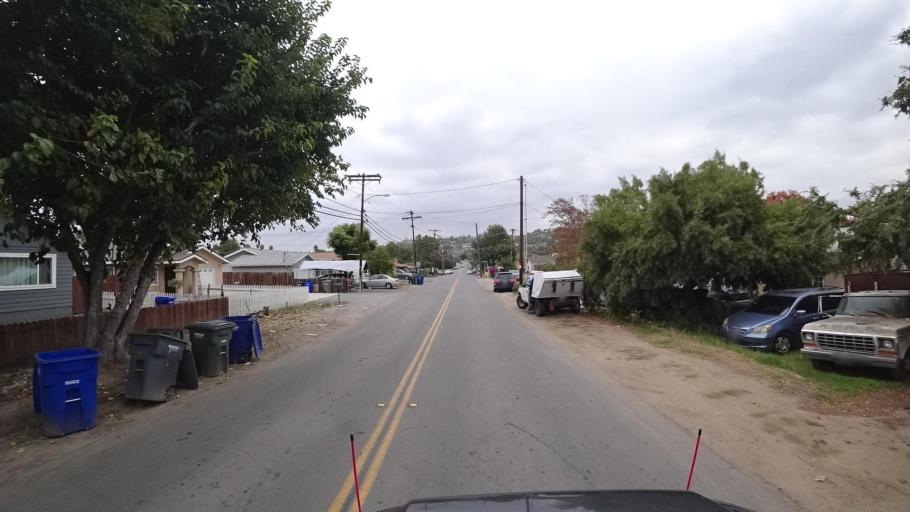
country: US
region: California
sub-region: San Diego County
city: Spring Valley
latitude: 32.7347
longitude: -117.0111
